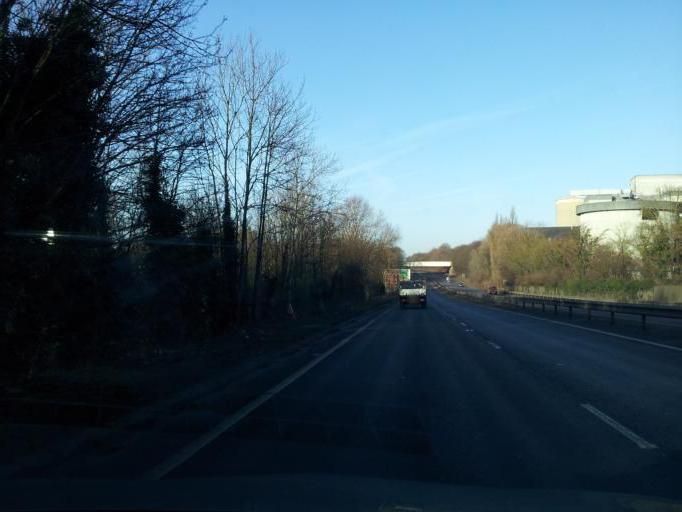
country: GB
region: England
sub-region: Suffolk
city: Bury St Edmunds
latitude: 52.2495
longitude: 0.7230
